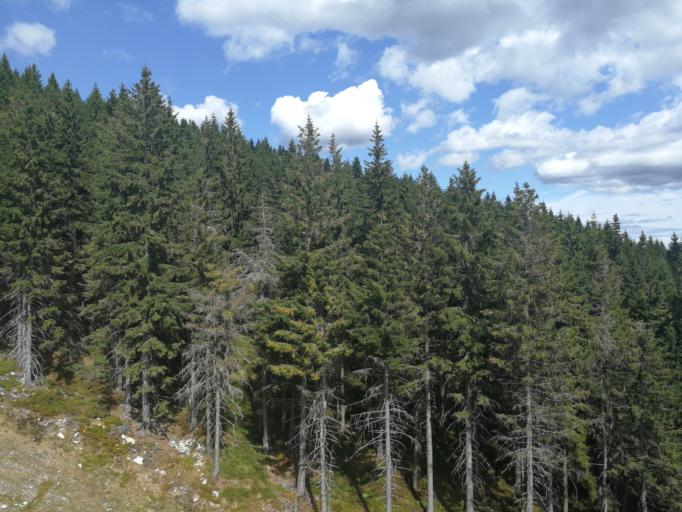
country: CZ
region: Kralovehradecky
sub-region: Okres Trutnov
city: Rudnik
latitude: 50.6435
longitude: 15.7568
